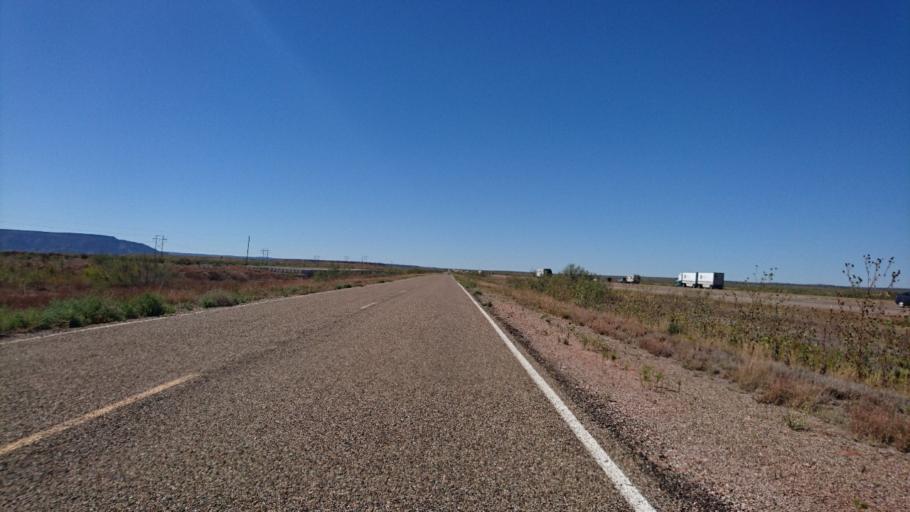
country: US
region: New Mexico
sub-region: Quay County
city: Tucumcari
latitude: 35.0904
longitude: -104.0810
